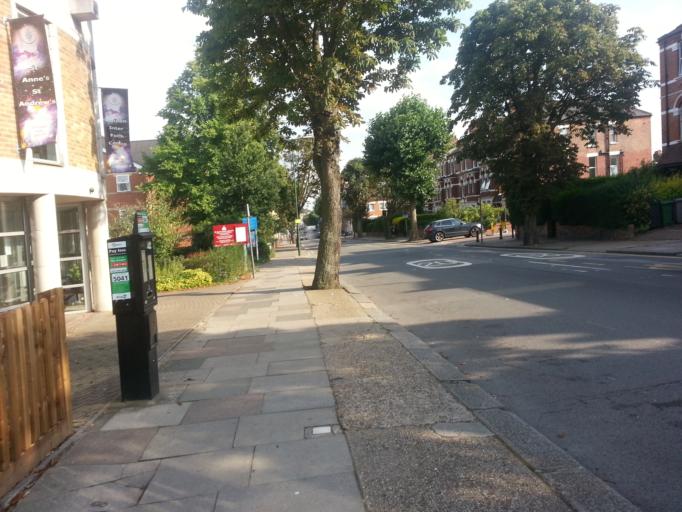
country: GB
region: England
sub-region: Greater London
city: Bayswater
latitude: 51.5387
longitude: -0.2077
